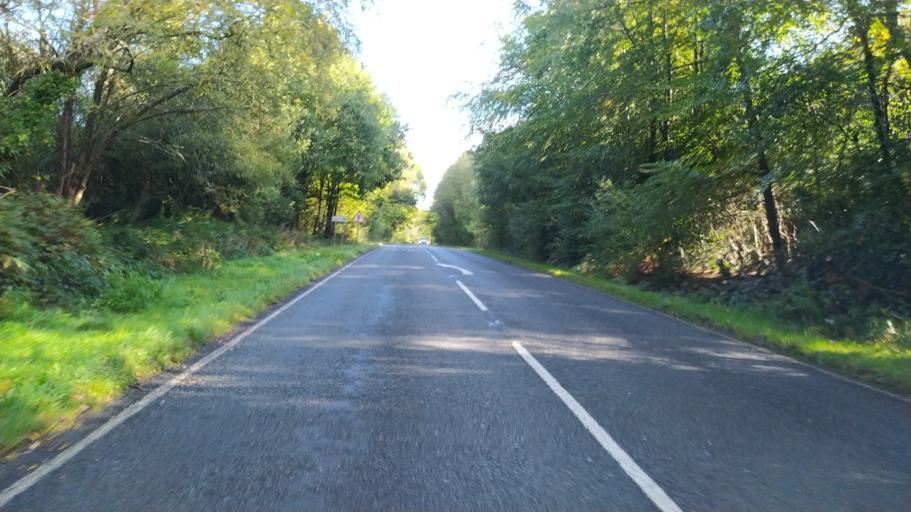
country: GB
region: England
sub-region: Hampshire
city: Lyndhurst
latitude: 50.8645
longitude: -1.5960
